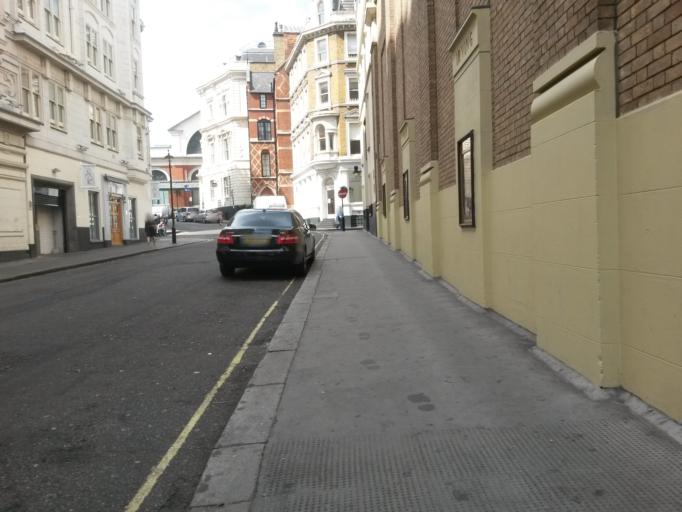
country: GB
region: England
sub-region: Greater London
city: London
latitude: 51.5112
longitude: -0.1203
